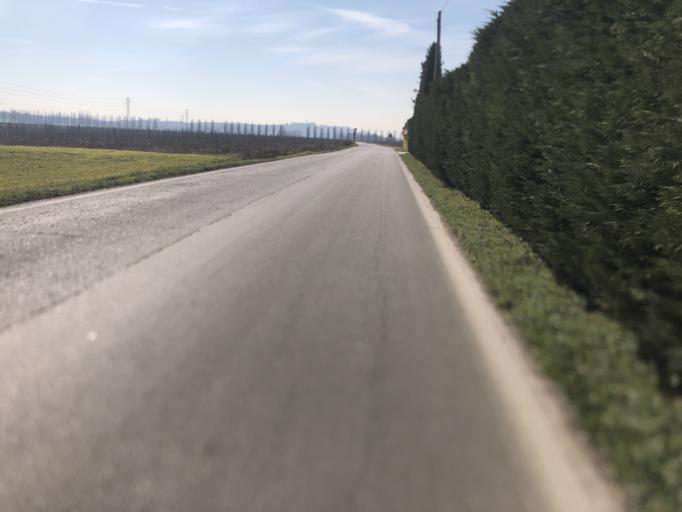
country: IT
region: Veneto
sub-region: Provincia di Verona
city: San Giorgio in Salici
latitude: 45.4106
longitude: 10.7998
